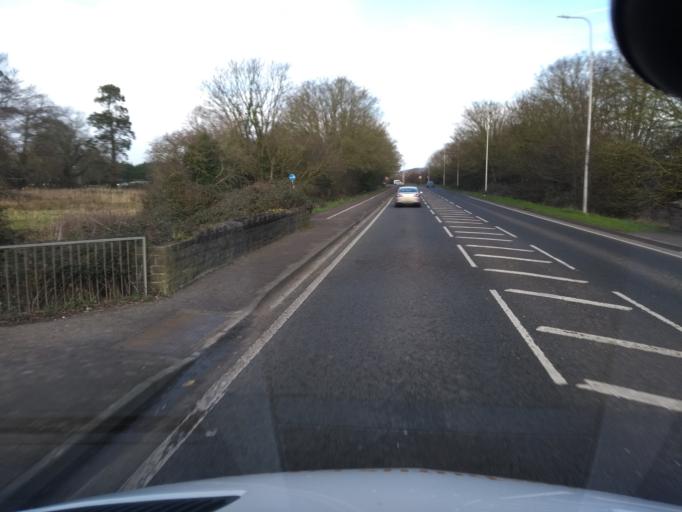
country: GB
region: England
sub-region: North Somerset
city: Weston-super-Mare
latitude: 51.3258
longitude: -2.9718
